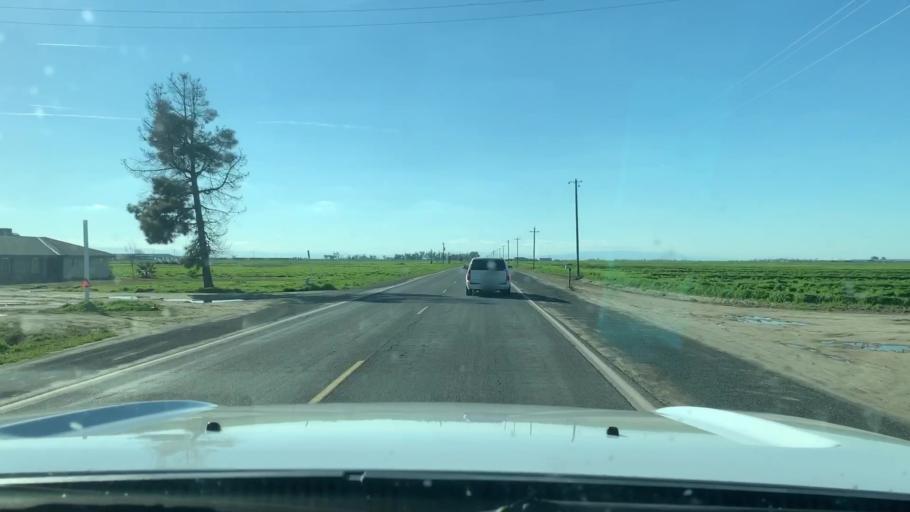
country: US
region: California
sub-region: Kings County
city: Home Garden
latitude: 36.2111
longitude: -119.6817
